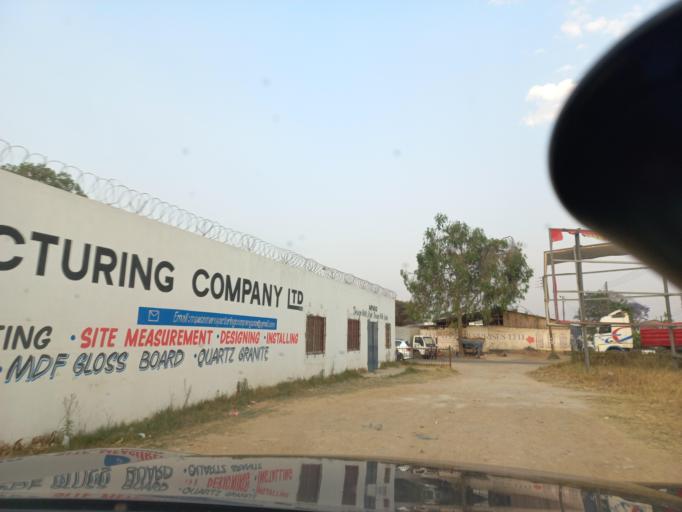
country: ZM
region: Lusaka
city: Lusaka
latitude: -15.3933
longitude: 28.2699
